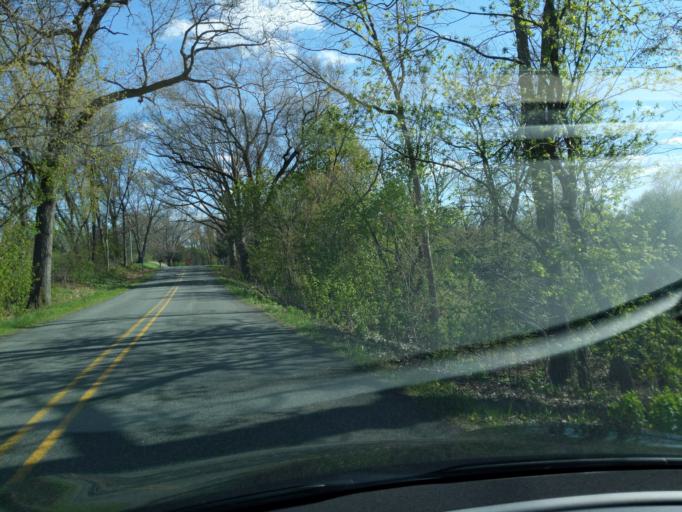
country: US
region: Michigan
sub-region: Jackson County
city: Spring Arbor
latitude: 42.3175
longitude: -84.5205
